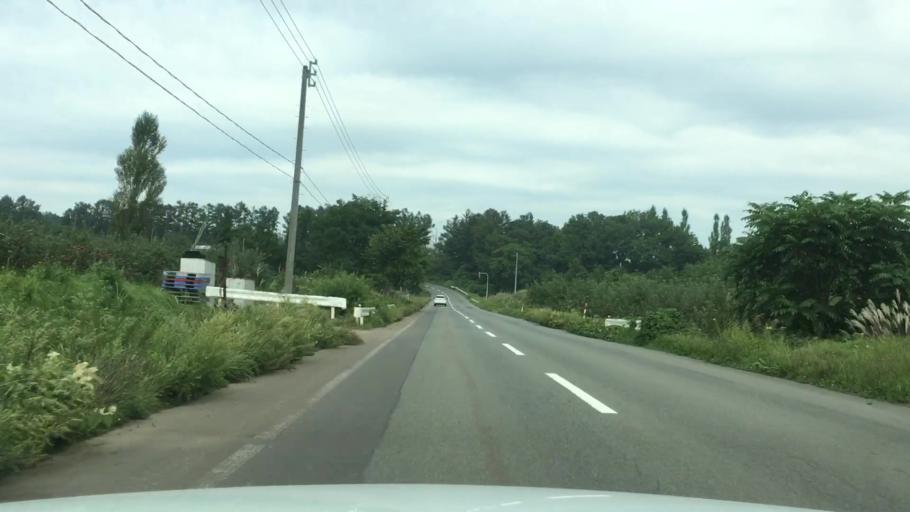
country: JP
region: Aomori
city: Shimokizukuri
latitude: 40.6835
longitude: 140.3700
